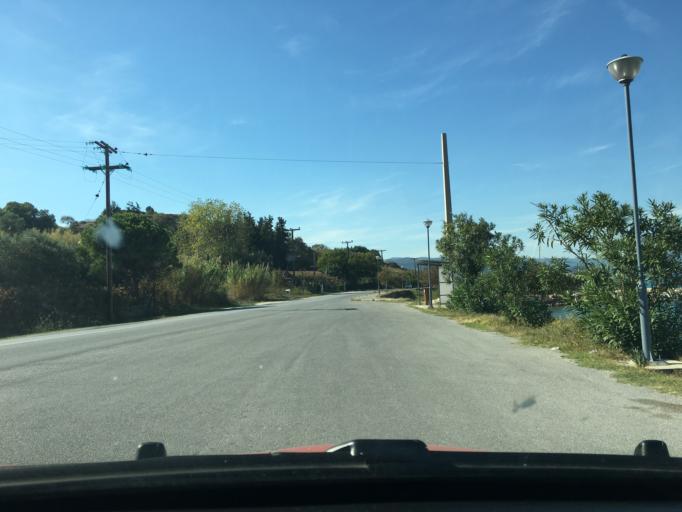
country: GR
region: Central Macedonia
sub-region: Nomos Chalkidikis
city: Ierissos
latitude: 40.3937
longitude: 23.8917
